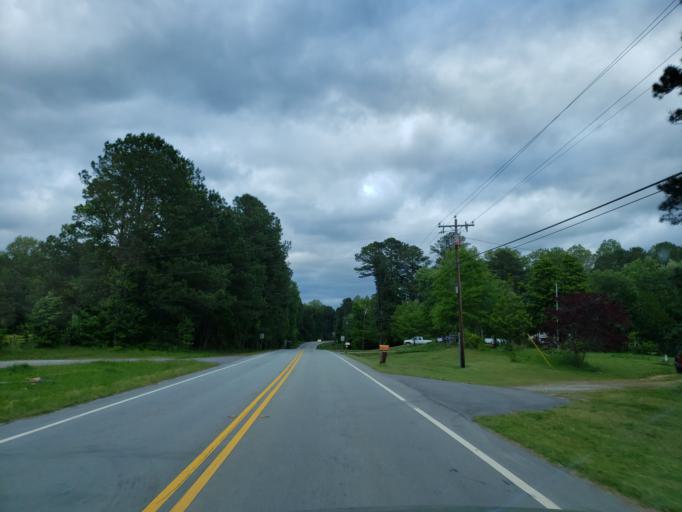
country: US
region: Georgia
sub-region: Paulding County
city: Dallas
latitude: 33.8708
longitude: -84.8705
